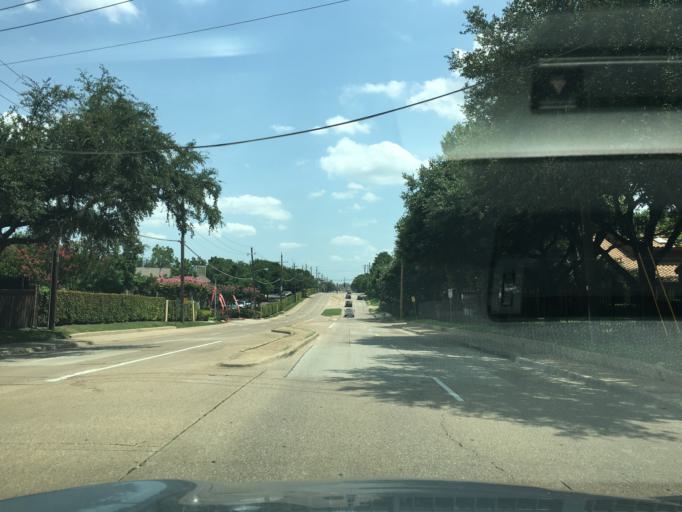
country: US
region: Texas
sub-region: Dallas County
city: Addison
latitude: 32.9422
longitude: -96.8143
